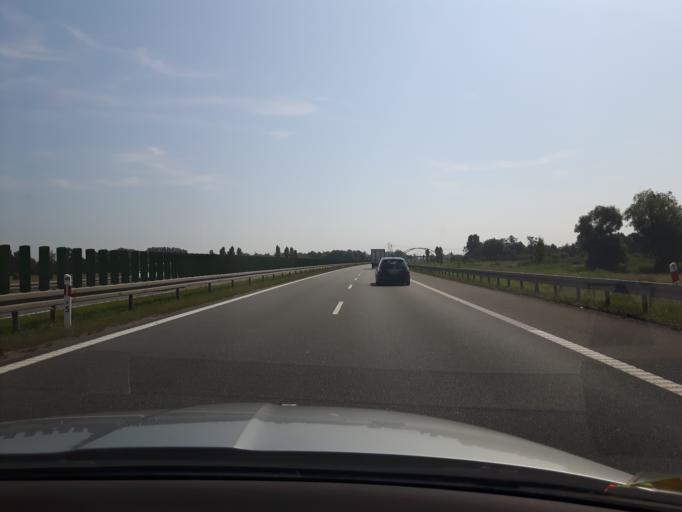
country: PL
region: Pomeranian Voivodeship
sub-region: Gdansk
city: Gdansk
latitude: 54.3203
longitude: 18.7332
